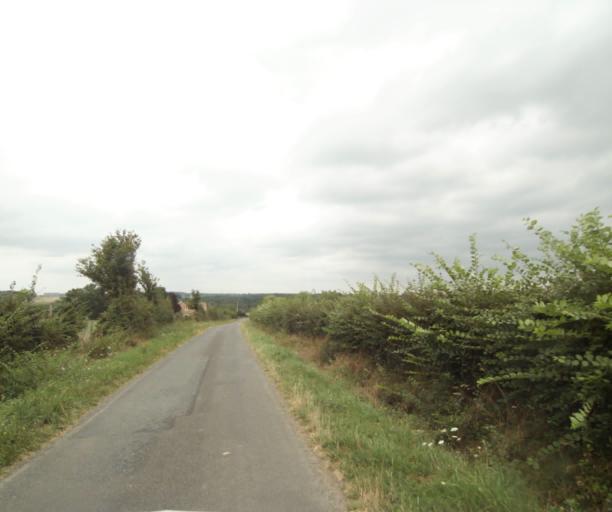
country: FR
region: Pays de la Loire
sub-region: Departement de la Sarthe
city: Juigne-sur-Sarthe
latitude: 47.8515
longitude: -0.2673
